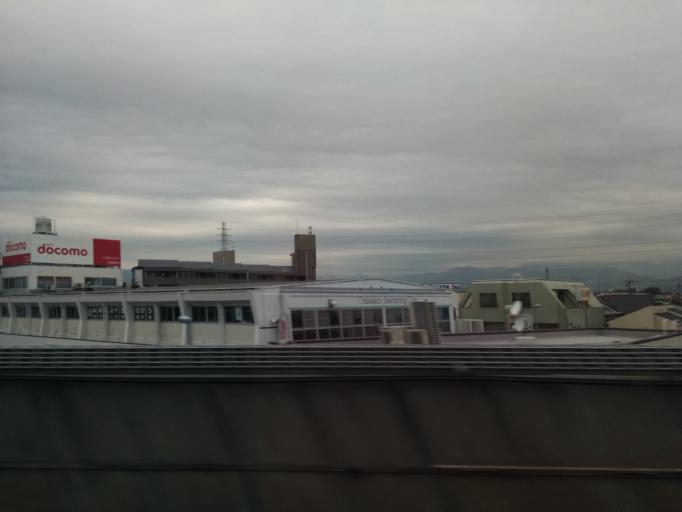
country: JP
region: Kanagawa
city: Odawara
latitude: 35.2788
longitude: 139.1793
